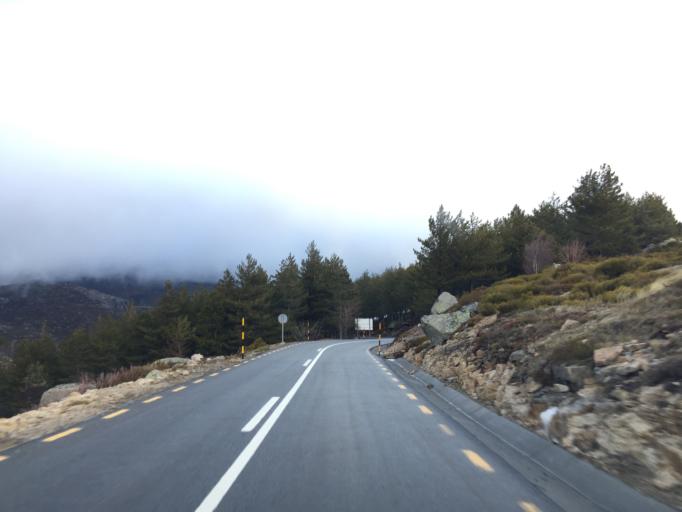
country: PT
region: Castelo Branco
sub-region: Covilha
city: Covilha
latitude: 40.3188
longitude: -7.5744
